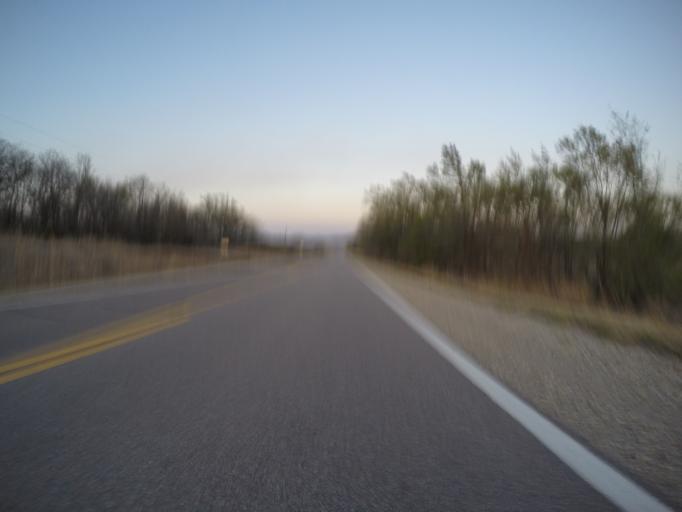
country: US
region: Kansas
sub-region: Riley County
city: Ogden
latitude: 39.1019
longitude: -96.6483
